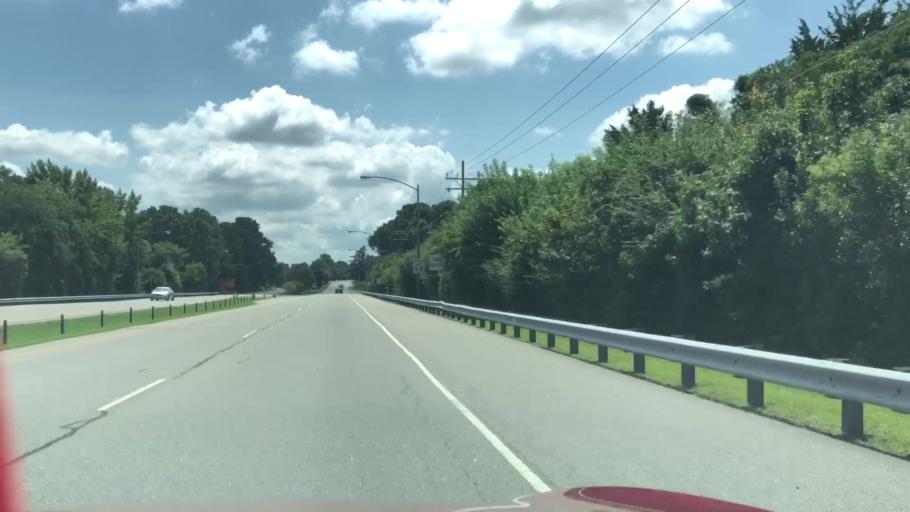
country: US
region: Virginia
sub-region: City of Virginia Beach
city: Virginia Beach
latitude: 36.9098
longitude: -76.1308
